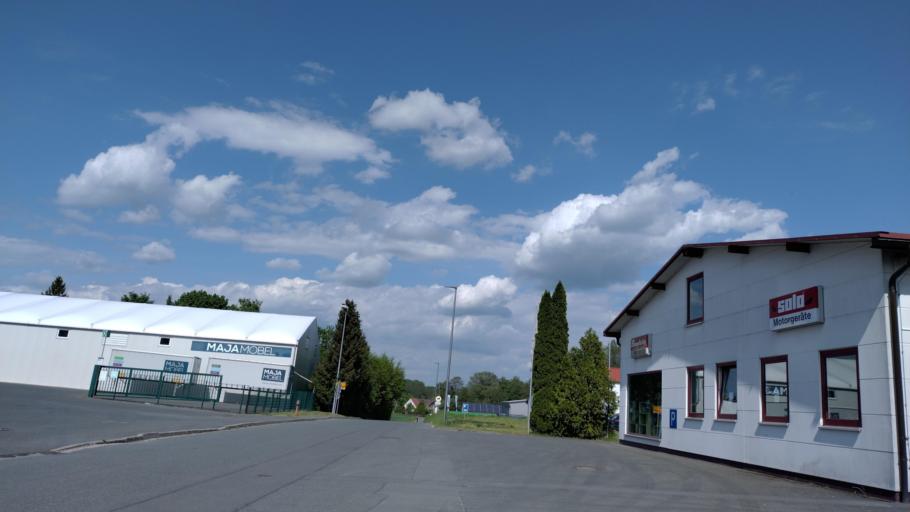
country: DE
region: Bavaria
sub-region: Upper Franconia
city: Kasendorf
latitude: 50.0401
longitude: 11.3611
